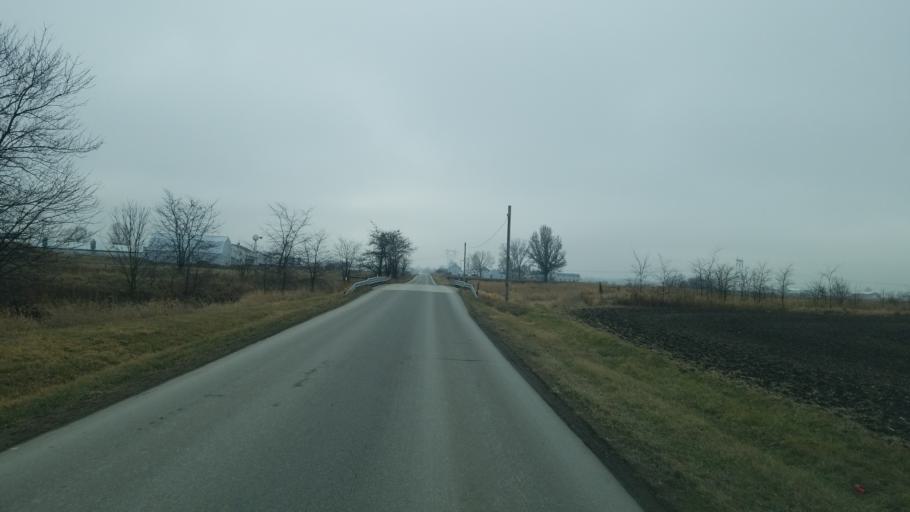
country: US
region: Indiana
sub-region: Adams County
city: Berne
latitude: 40.6792
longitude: -84.8981
